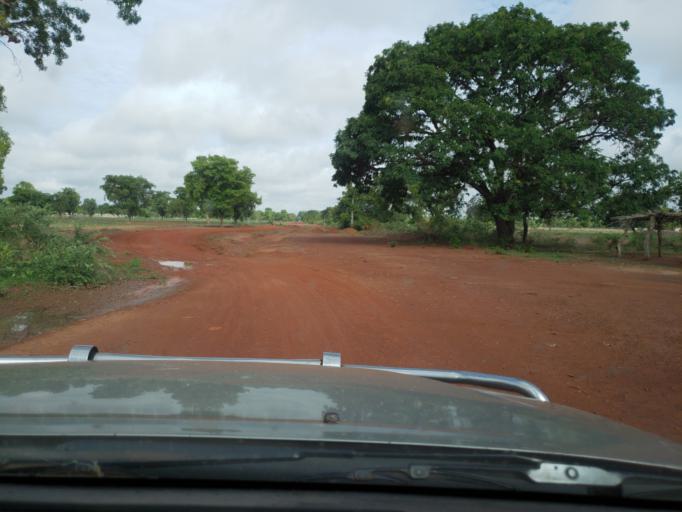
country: ML
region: Sikasso
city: Koutiala
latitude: 12.3925
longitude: -6.0056
